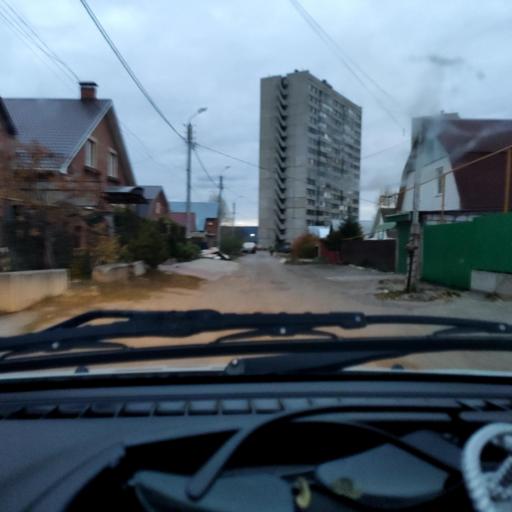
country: RU
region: Samara
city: Zhigulevsk
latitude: 53.4817
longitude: 49.5259
